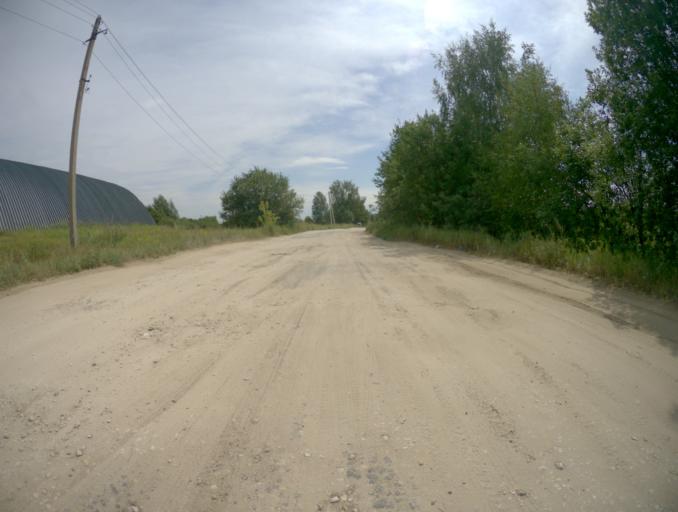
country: RU
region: Vladimir
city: Raduzhnyy
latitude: 56.0270
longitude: 40.3075
